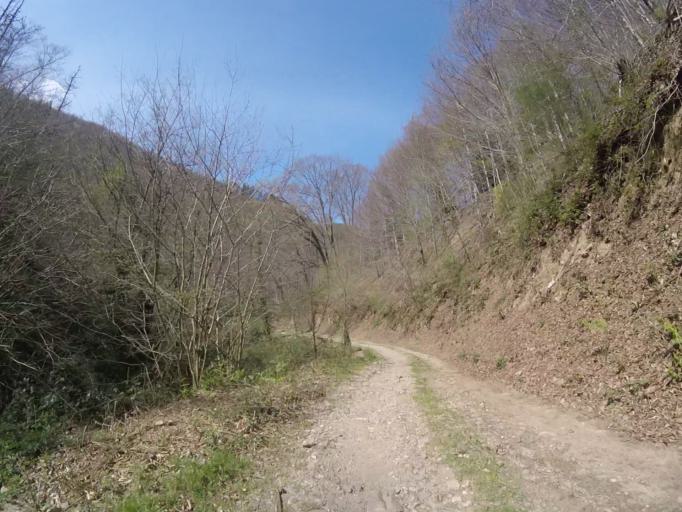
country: ES
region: Basque Country
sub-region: Provincia de Guipuzcoa
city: Irun
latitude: 43.2593
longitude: -1.8086
